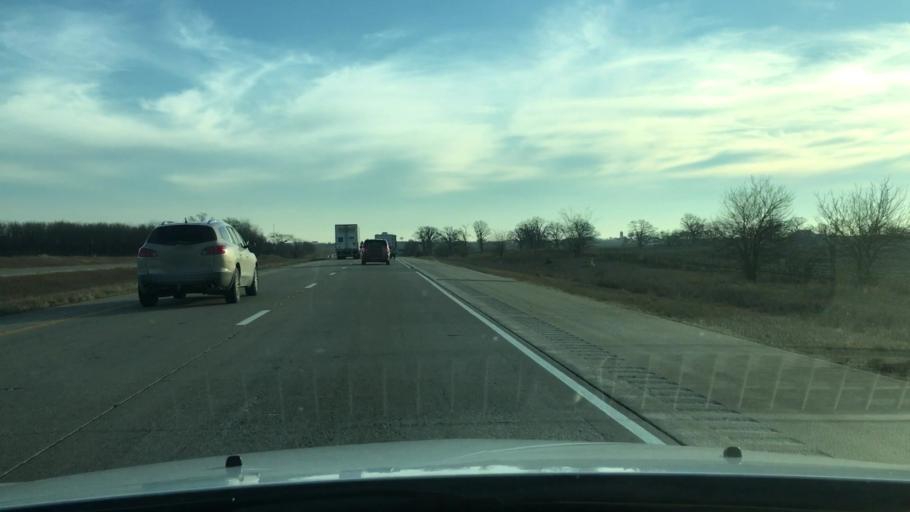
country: US
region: Illinois
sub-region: Woodford County
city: El Paso
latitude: 40.7691
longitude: -89.0349
